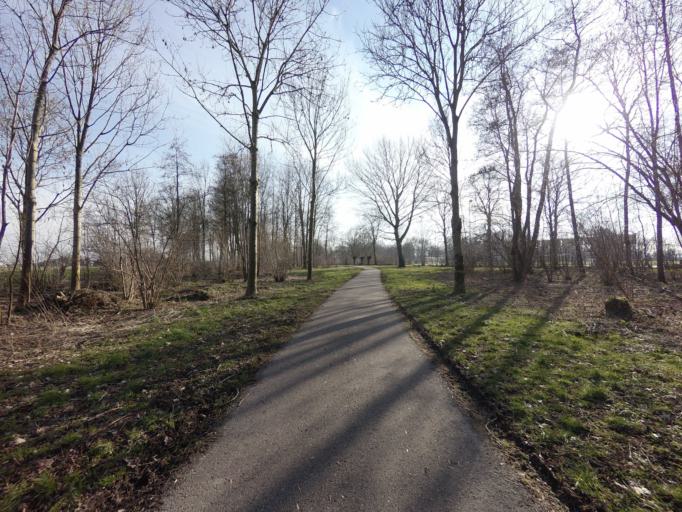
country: NL
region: South Holland
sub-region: Gemeente Giessenlanden
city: Giessenburg
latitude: 51.8494
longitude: 4.8972
